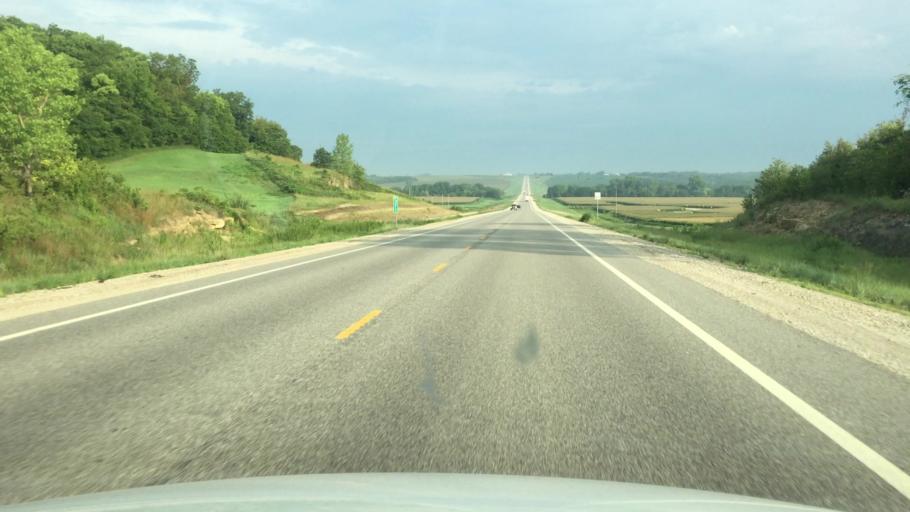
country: US
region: Kansas
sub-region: Doniphan County
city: Highland
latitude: 39.8097
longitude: -95.1922
